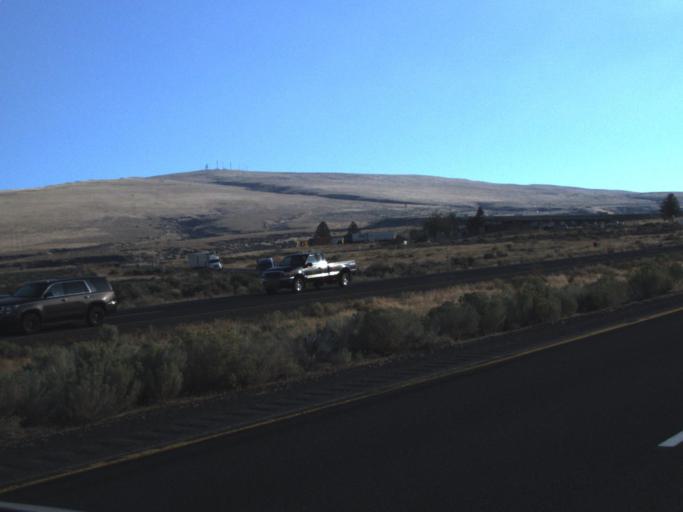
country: US
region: Washington
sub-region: Yakima County
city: Terrace Heights
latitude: 46.6948
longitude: -120.4459
